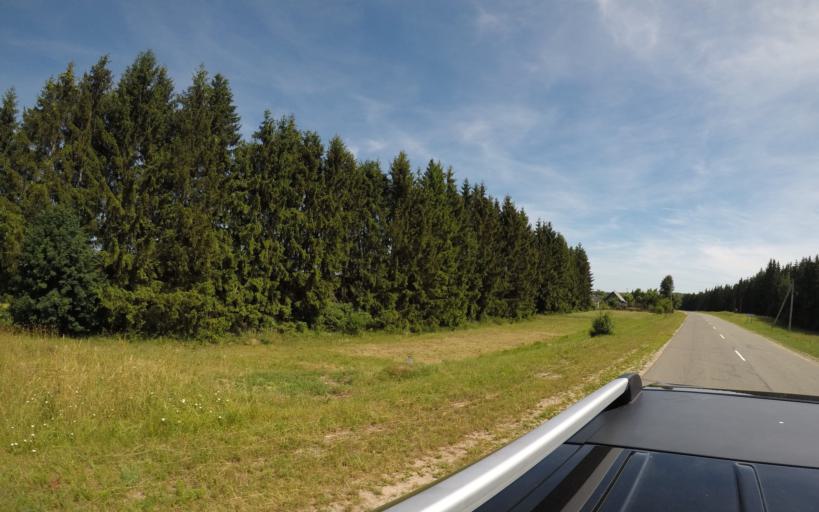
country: BY
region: Grodnenskaya
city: Hal'shany
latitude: 54.2659
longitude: 25.9933
